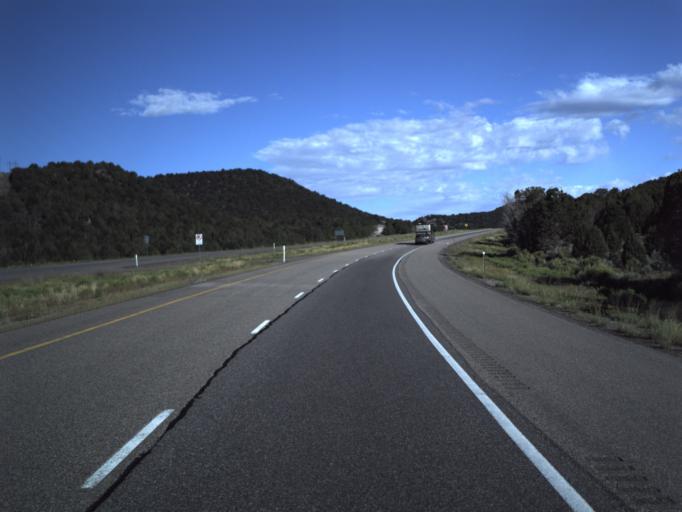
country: US
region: Utah
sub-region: Beaver County
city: Beaver
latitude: 38.5803
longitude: -112.4815
